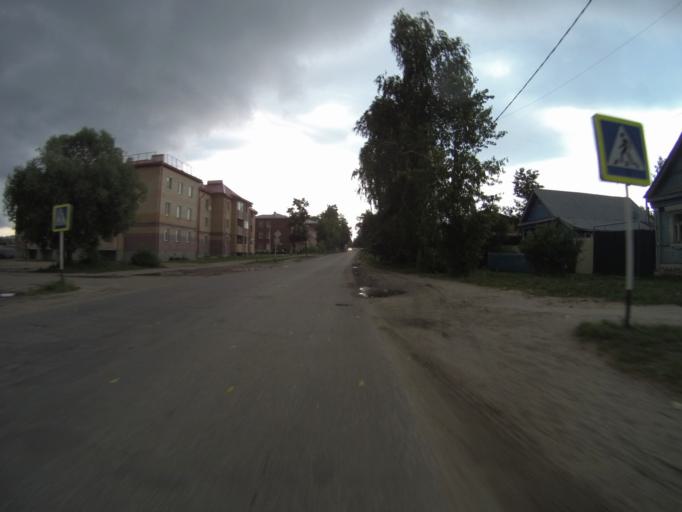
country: RU
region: Vladimir
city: Kameshkovo
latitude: 56.3446
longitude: 40.9917
